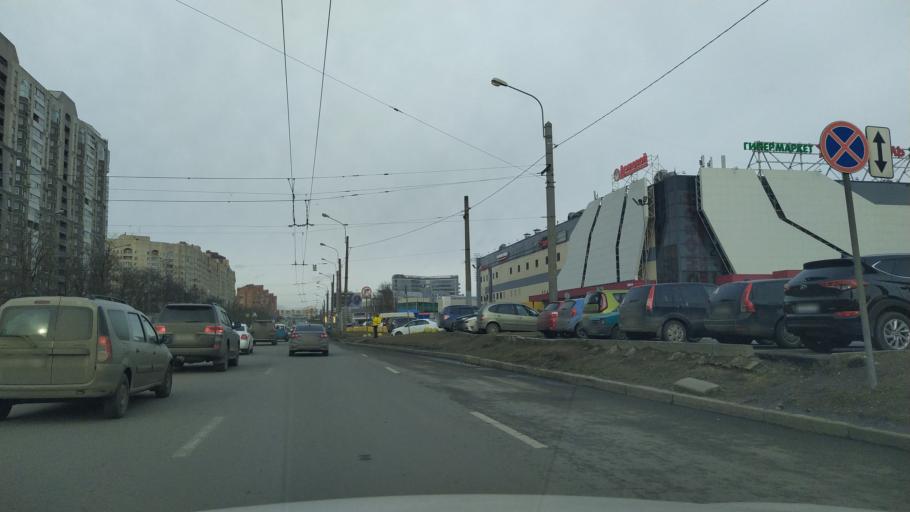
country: RU
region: Leningrad
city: Chernaya Rechka
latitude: 60.0042
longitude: 30.2978
